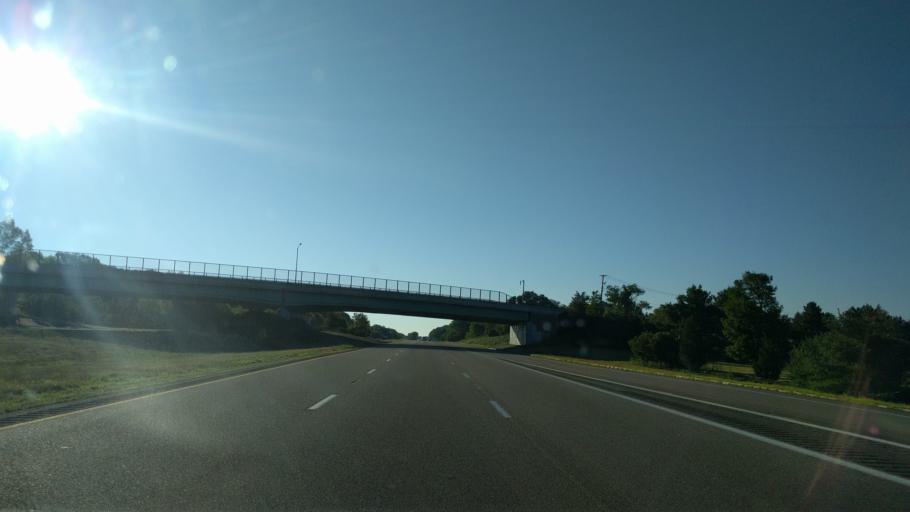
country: US
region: Massachusetts
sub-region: Bristol County
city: Mansfield Center
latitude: 42.0008
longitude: -71.2127
